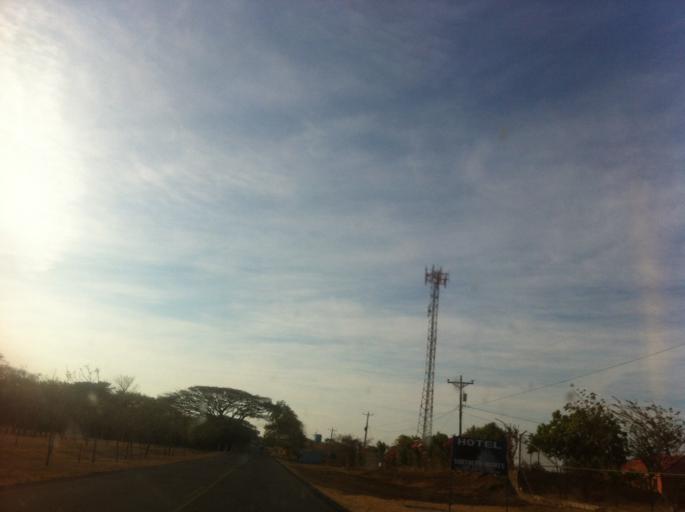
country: NI
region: Rivas
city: Rivas
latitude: 11.3492
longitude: -85.7376
